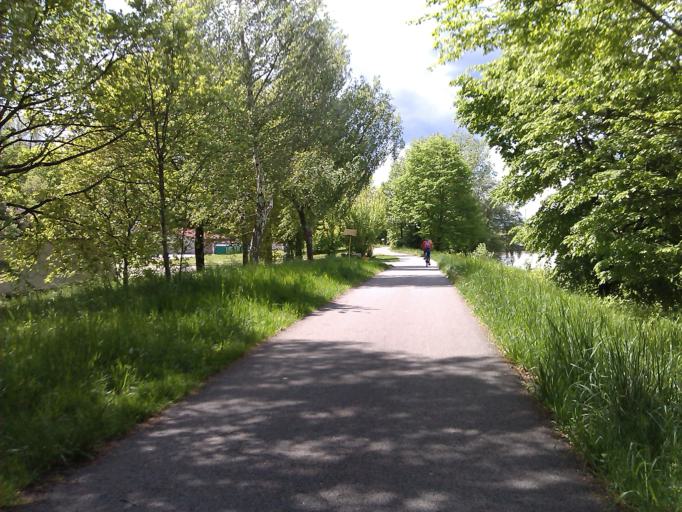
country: FR
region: Franche-Comte
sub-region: Departement du Doubs
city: Sochaux
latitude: 47.5038
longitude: 6.8296
